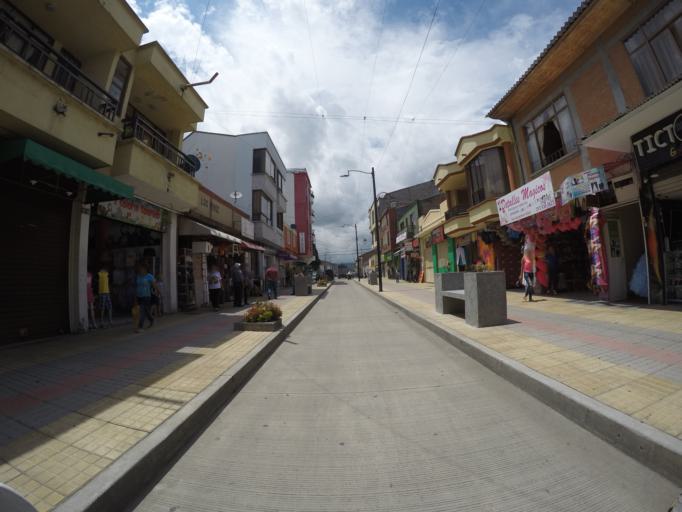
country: CO
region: Quindio
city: Quimbaya
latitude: 4.6226
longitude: -75.7612
